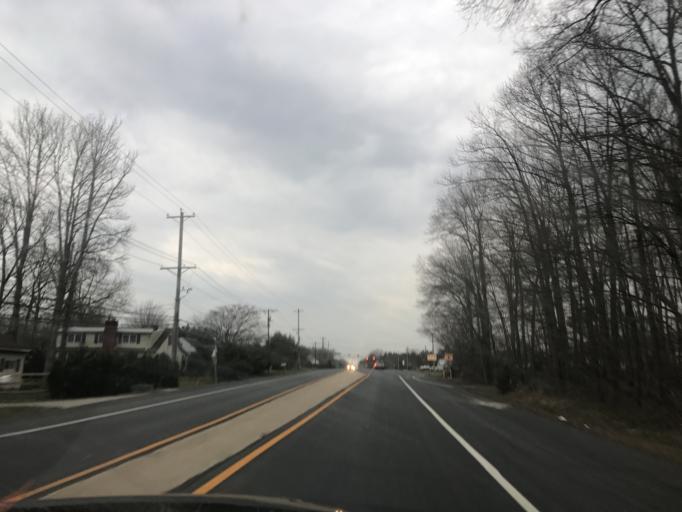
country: US
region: Delaware
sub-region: New Castle County
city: Glasgow
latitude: 39.6270
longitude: -75.7700
